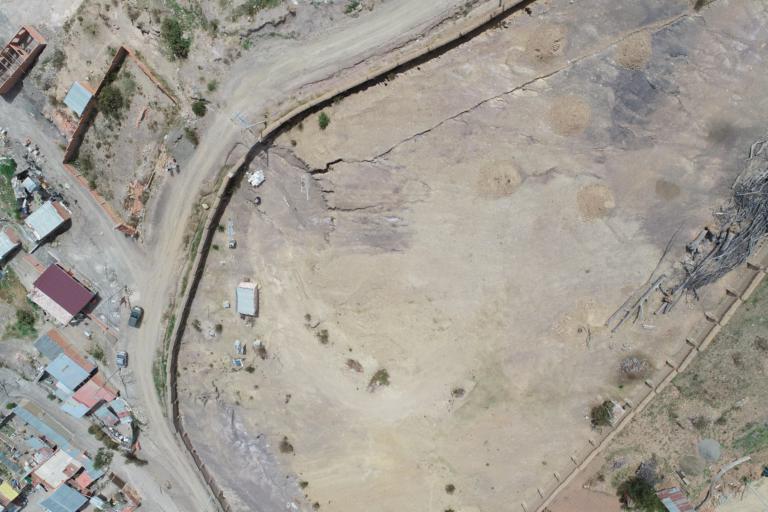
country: BO
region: La Paz
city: La Paz
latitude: -16.5539
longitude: -68.0509
